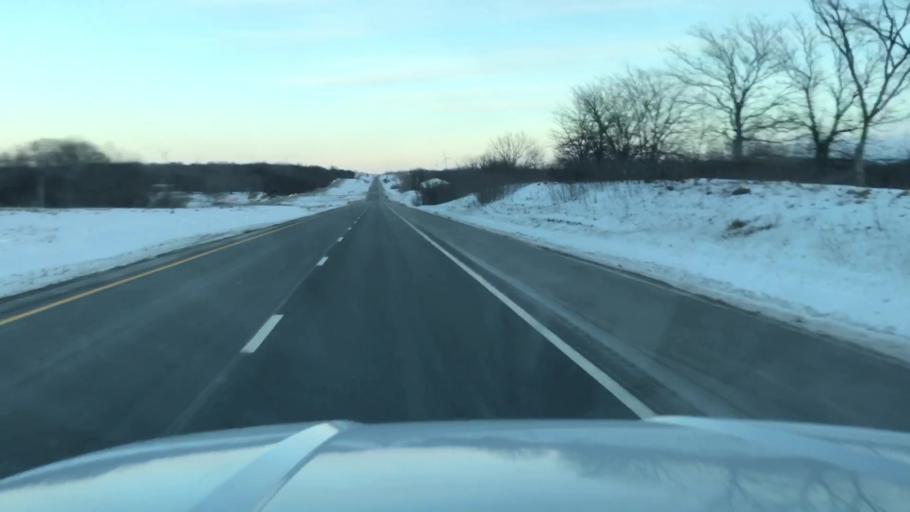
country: US
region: Missouri
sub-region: DeKalb County
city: Maysville
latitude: 39.7620
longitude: -94.4901
